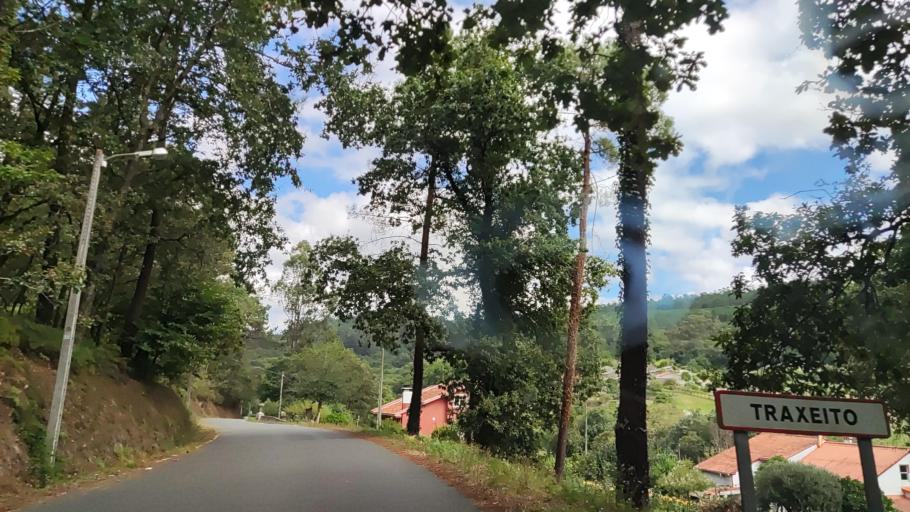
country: ES
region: Galicia
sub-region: Provincia da Coruna
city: Rois
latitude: 42.7390
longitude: -8.7003
